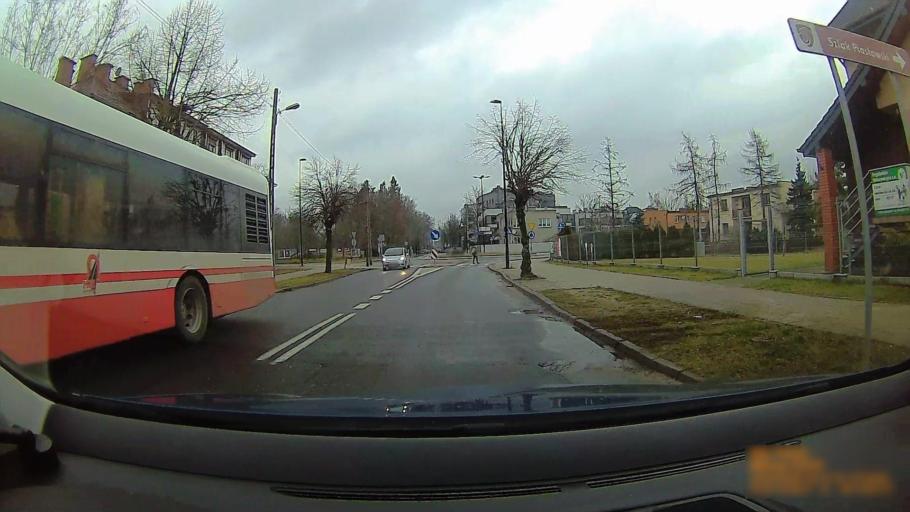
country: PL
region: Greater Poland Voivodeship
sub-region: Konin
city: Konin
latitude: 52.2082
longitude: 18.2465
